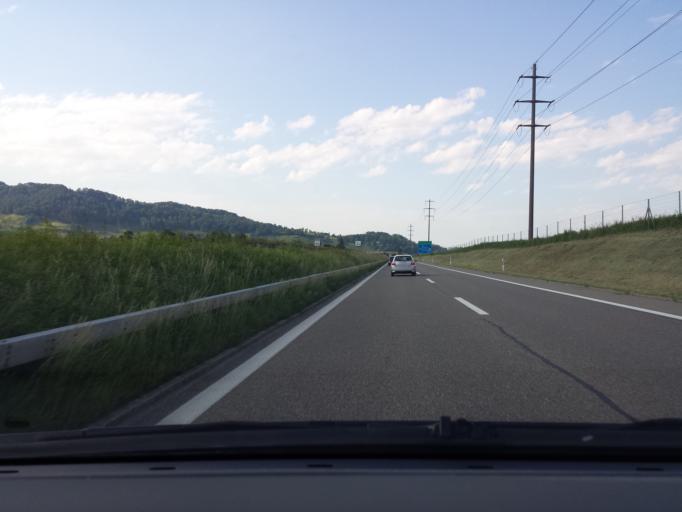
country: AT
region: Vorarlberg
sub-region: Politischer Bezirk Dornbirn
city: Lustenau
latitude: 47.4201
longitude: 9.6469
